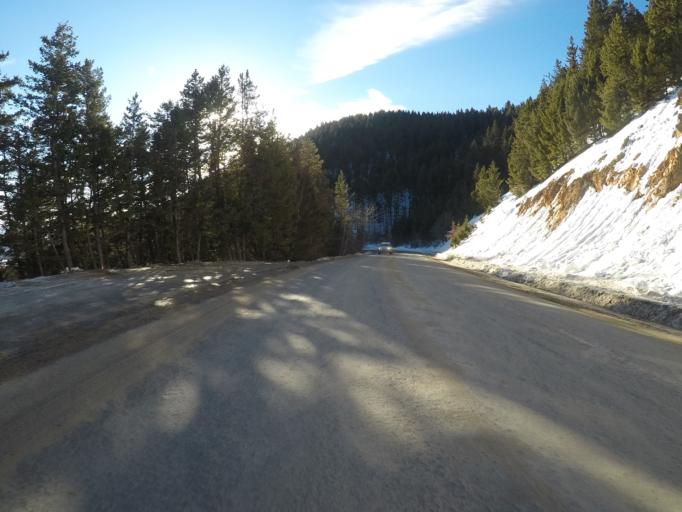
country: US
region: Montana
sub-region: Carbon County
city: Red Lodge
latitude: 45.1710
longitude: -109.3138
